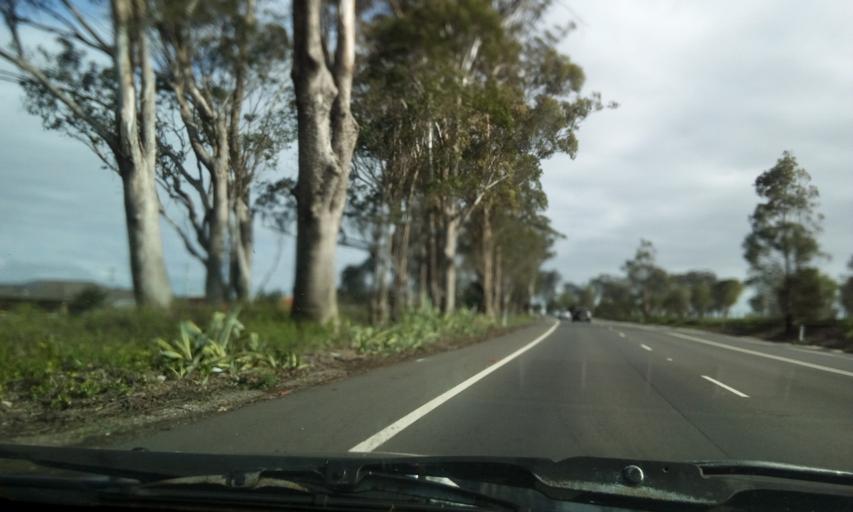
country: AU
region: New South Wales
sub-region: Wollondilly
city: Douglas Park
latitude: -34.1667
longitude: 150.7895
